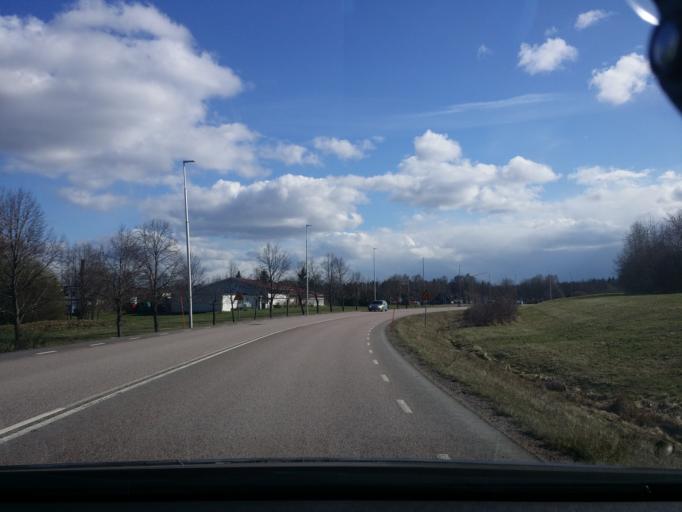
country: SE
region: Vaestmanland
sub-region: Sala Kommun
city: Sala
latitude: 59.9344
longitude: 16.5738
